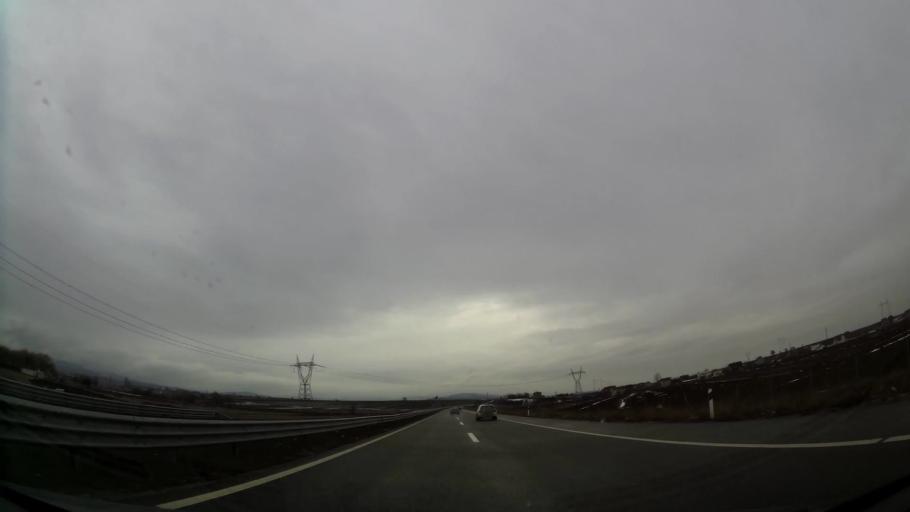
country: XK
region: Pristina
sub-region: Lipjan
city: Lipljan
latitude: 42.5107
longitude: 21.1794
